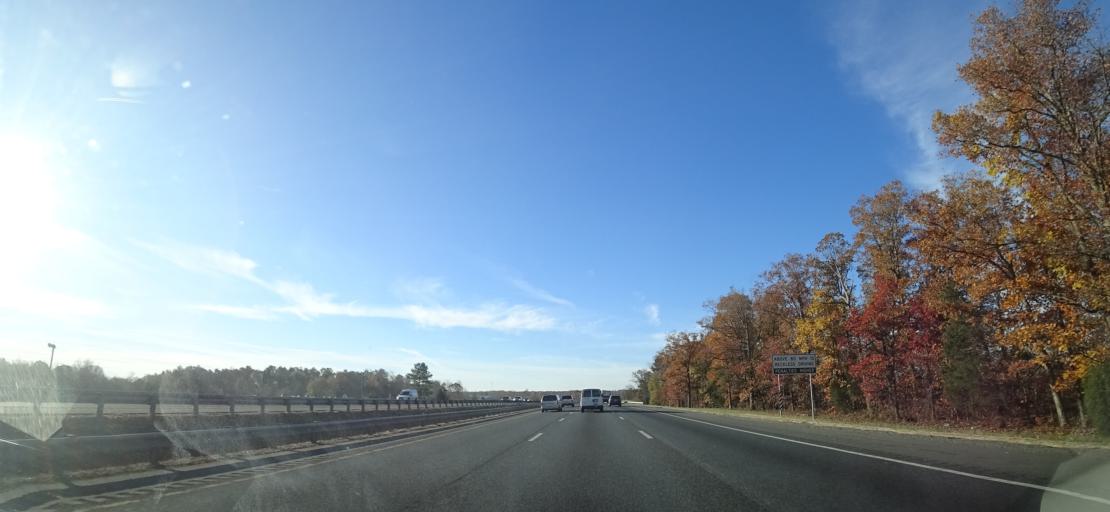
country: US
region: Virginia
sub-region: Spotsylvania County
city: Spotsylvania Courthouse
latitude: 38.1258
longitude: -77.5147
